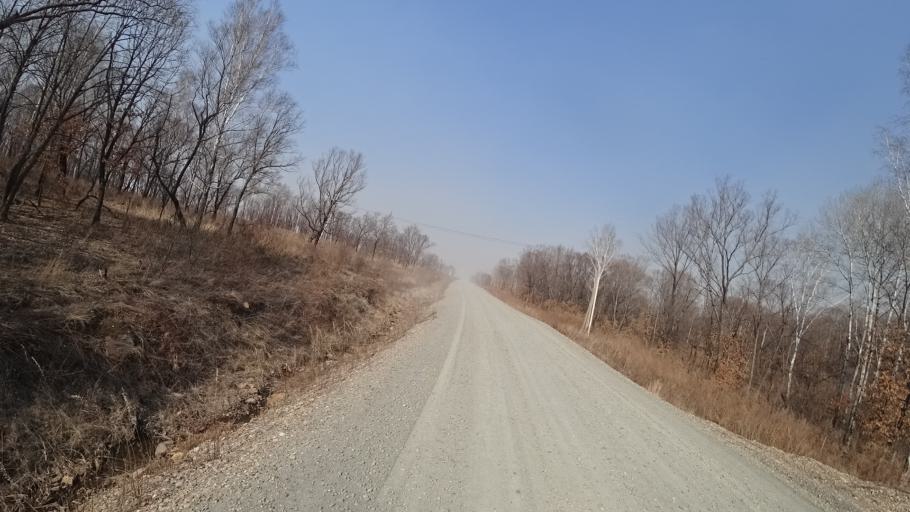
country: RU
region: Amur
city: Novobureyskiy
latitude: 49.8001
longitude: 129.9592
